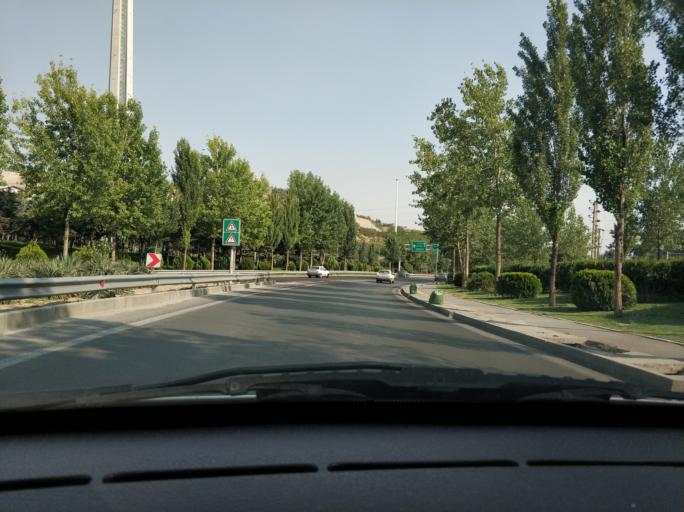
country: IR
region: Tehran
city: Tehran
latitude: 35.7482
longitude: 51.3697
